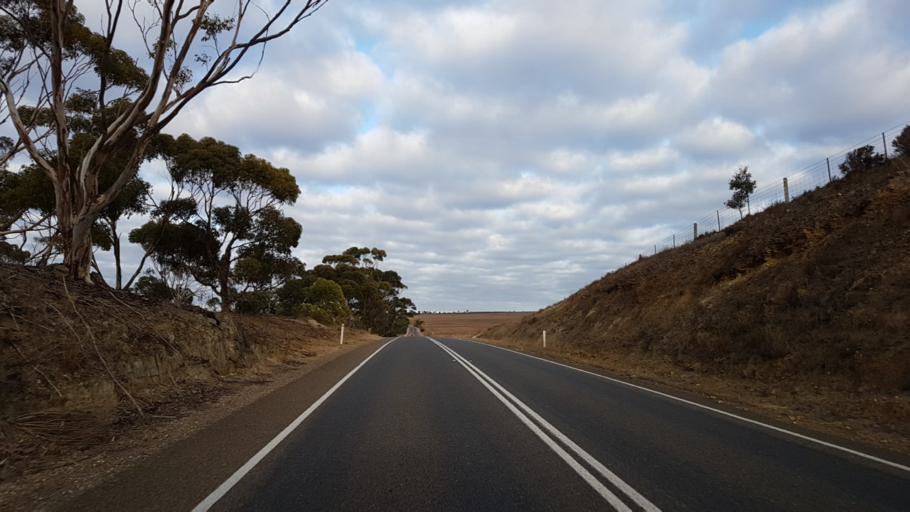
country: AU
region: South Australia
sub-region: Mount Barker
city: Callington
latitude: -35.1795
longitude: 139.0123
